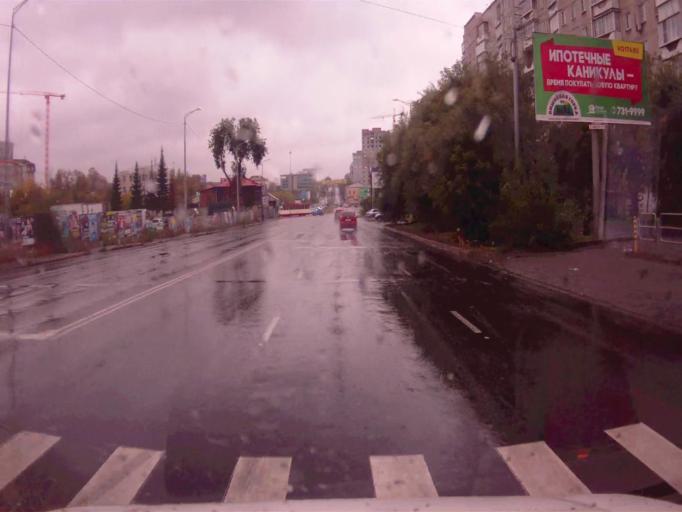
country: RU
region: Chelyabinsk
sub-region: Gorod Chelyabinsk
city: Chelyabinsk
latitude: 55.1641
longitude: 61.4162
